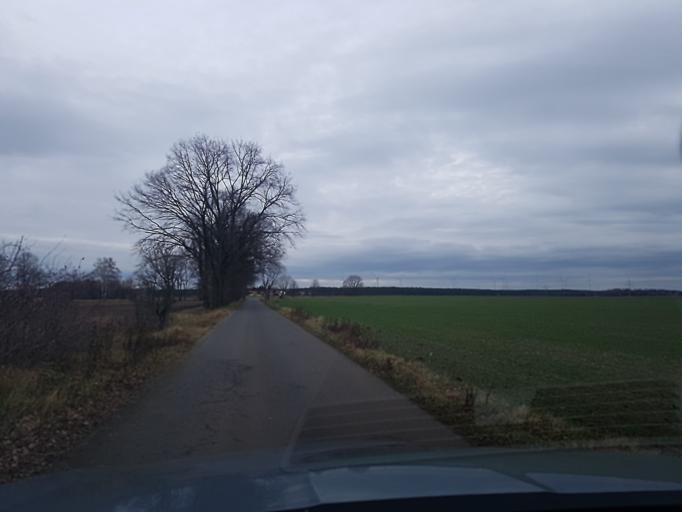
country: DE
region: Brandenburg
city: Schilda
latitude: 51.6247
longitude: 13.3529
